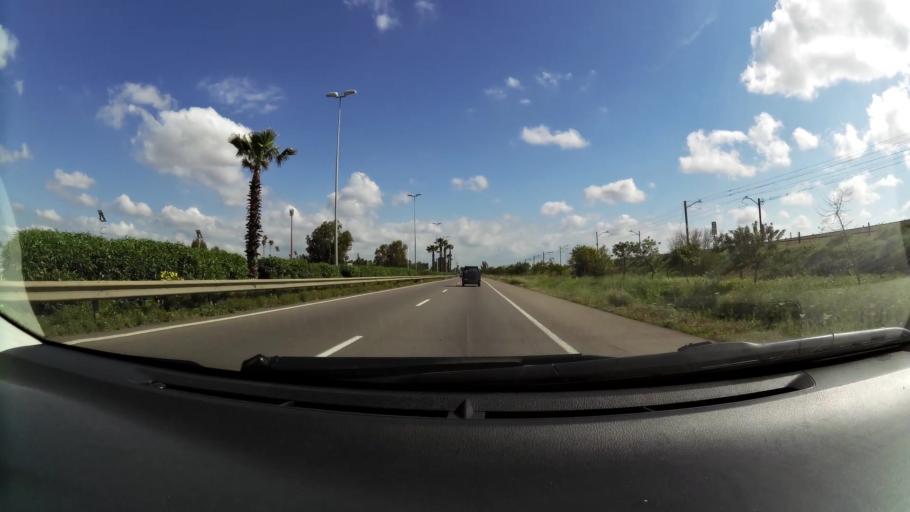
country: MA
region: Chaouia-Ouardigha
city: Nouaseur
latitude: 33.4075
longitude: -7.6250
